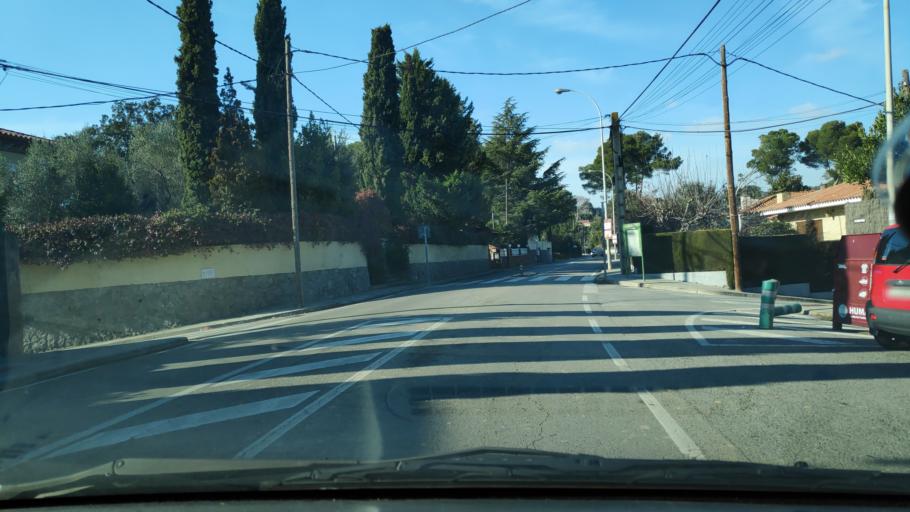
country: ES
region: Catalonia
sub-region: Provincia de Barcelona
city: Sant Cugat del Valles
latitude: 41.4960
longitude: 2.0892
